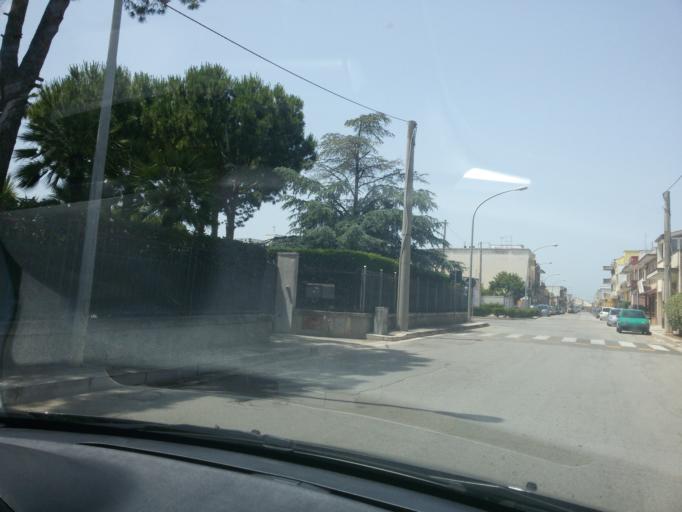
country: IT
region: Apulia
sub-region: Provincia di Brindisi
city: Mesagne
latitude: 40.5515
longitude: 17.8152
